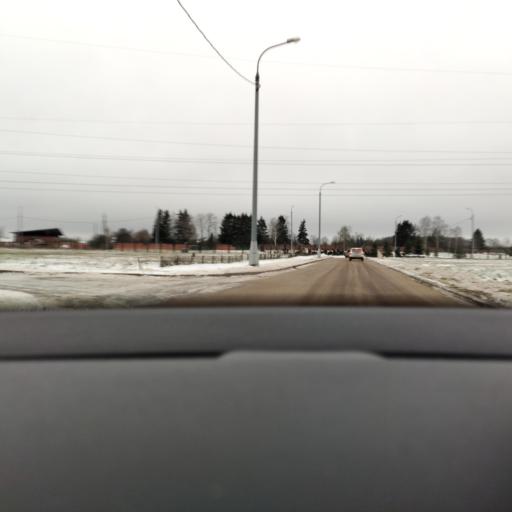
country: RU
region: Moskovskaya
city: Alabushevo
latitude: 56.0131
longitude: 37.1403
